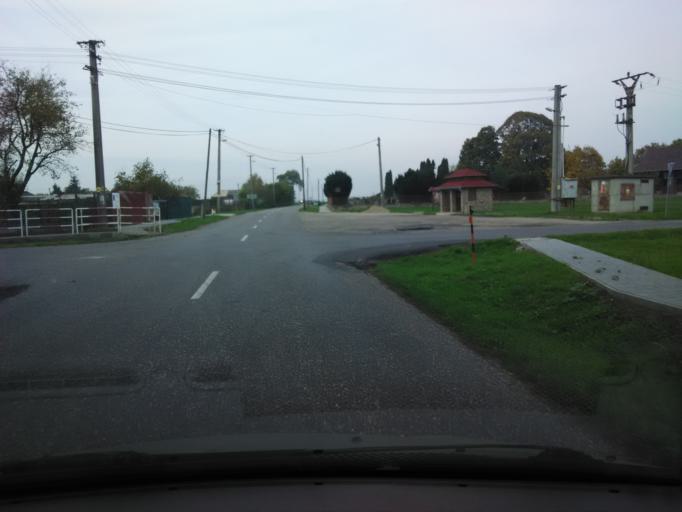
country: SK
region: Nitriansky
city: Levice
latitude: 48.1383
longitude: 18.5228
